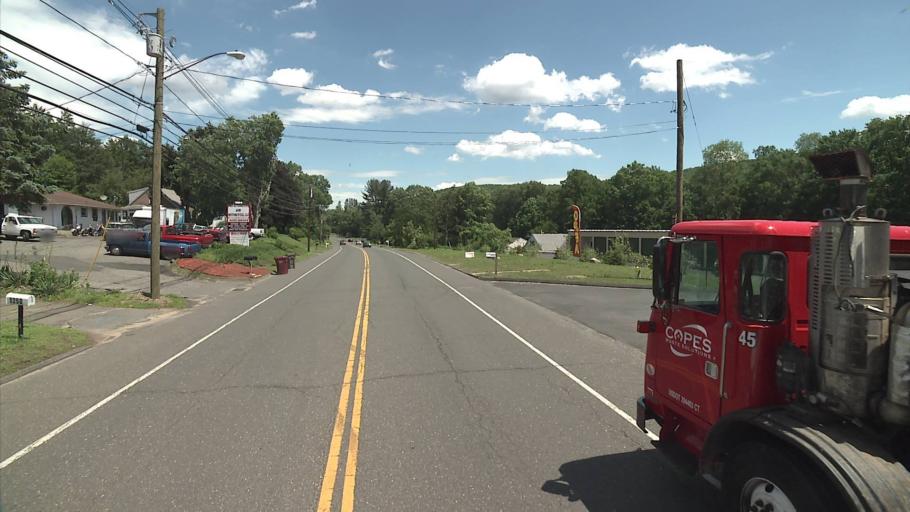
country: US
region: Connecticut
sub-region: New Haven County
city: Naugatuck
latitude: 41.4677
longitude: -73.0193
